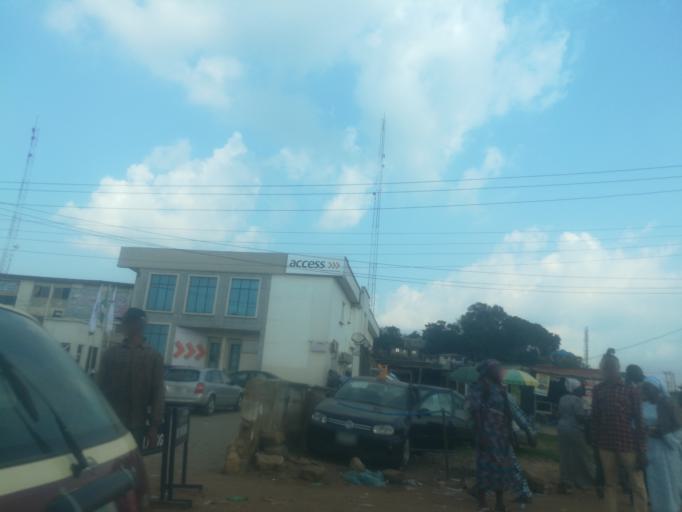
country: NG
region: Oyo
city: Moniya
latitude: 7.4725
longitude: 3.9134
